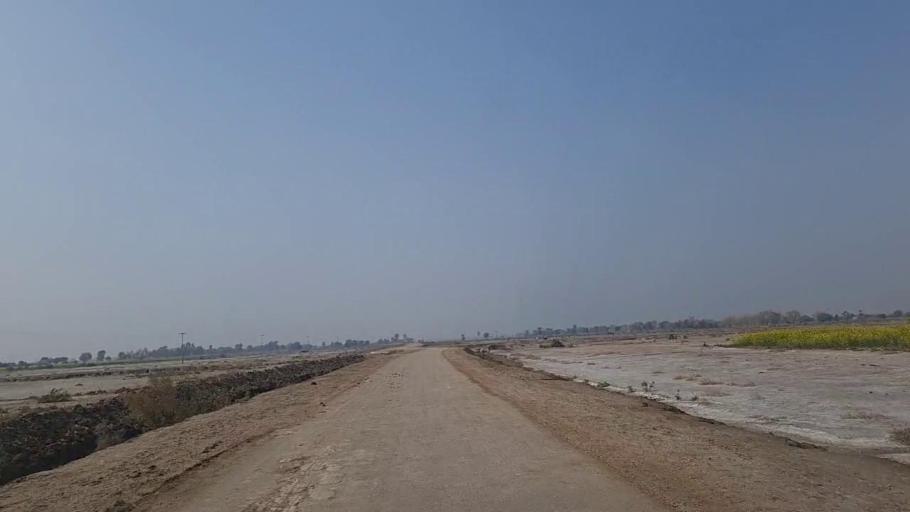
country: PK
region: Sindh
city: Nawabshah
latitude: 26.3601
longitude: 68.4316
